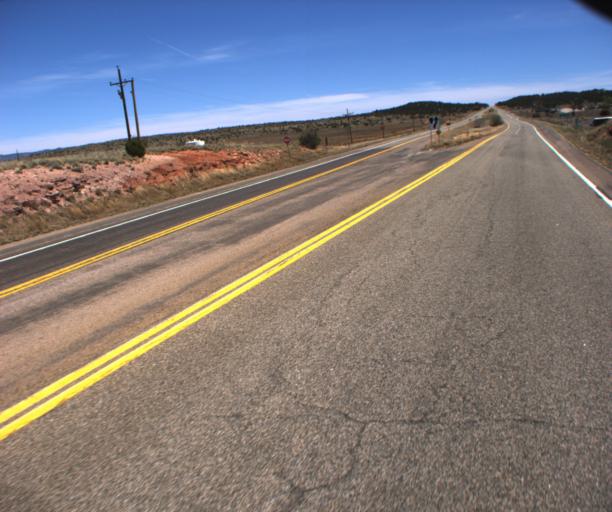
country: US
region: Arizona
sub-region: Mohave County
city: Peach Springs
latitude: 35.5319
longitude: -113.2381
